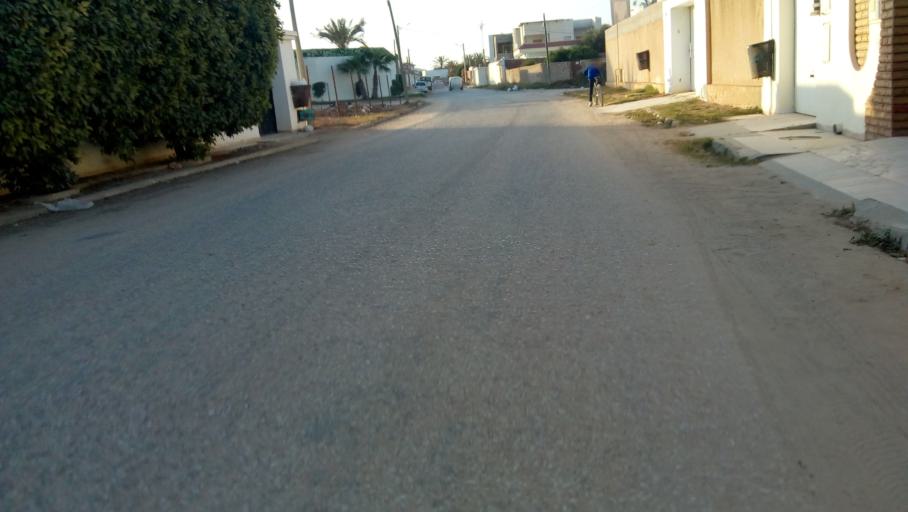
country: TN
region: Safaqis
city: Sfax
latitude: 34.7527
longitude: 10.7339
